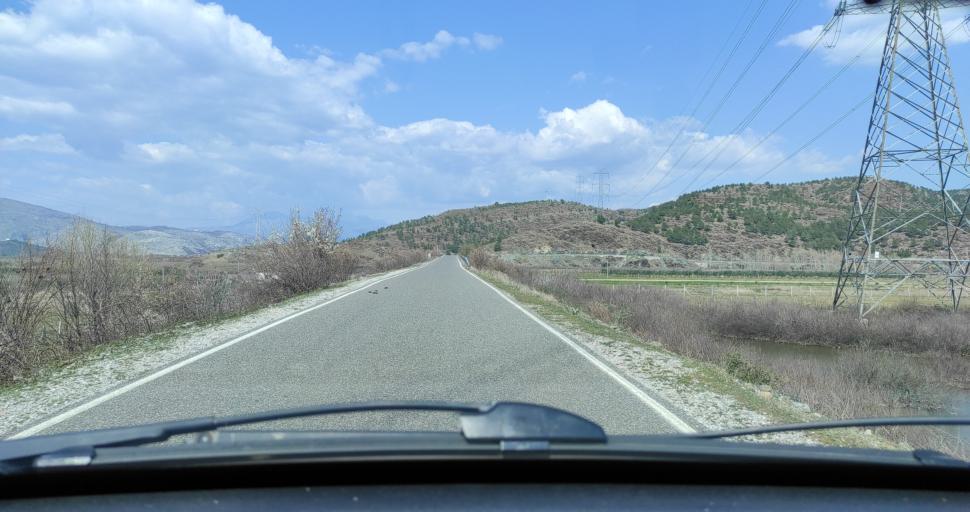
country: AL
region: Shkoder
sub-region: Rrethi i Shkodres
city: Hajmel
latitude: 41.9746
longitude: 19.6448
